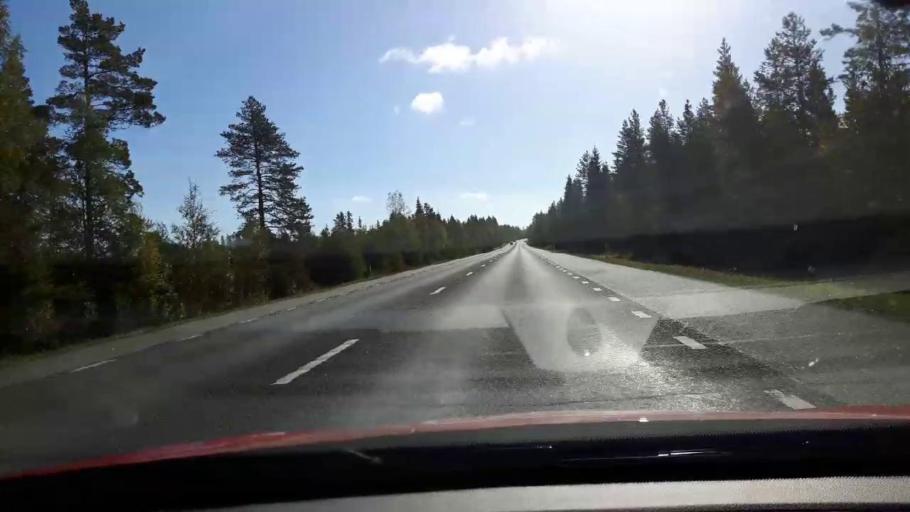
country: SE
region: Jaemtland
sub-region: Braecke Kommun
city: Braecke
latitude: 62.7084
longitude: 15.4865
